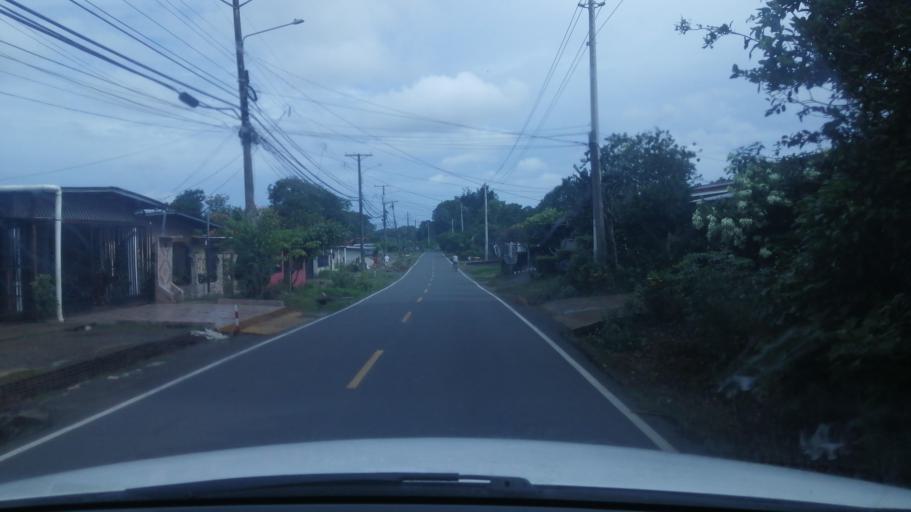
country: PA
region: Chiriqui
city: David
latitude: 8.4144
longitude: -82.4265
